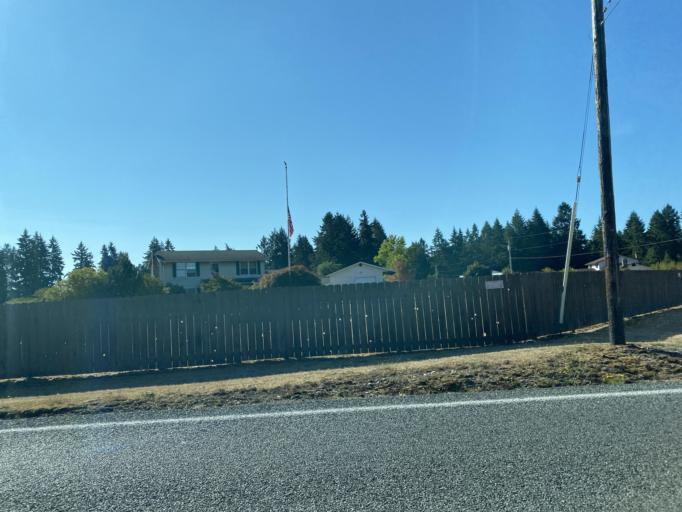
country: US
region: Washington
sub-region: Thurston County
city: Tanglewilde-Thompson Place
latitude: 47.0110
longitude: -122.7336
